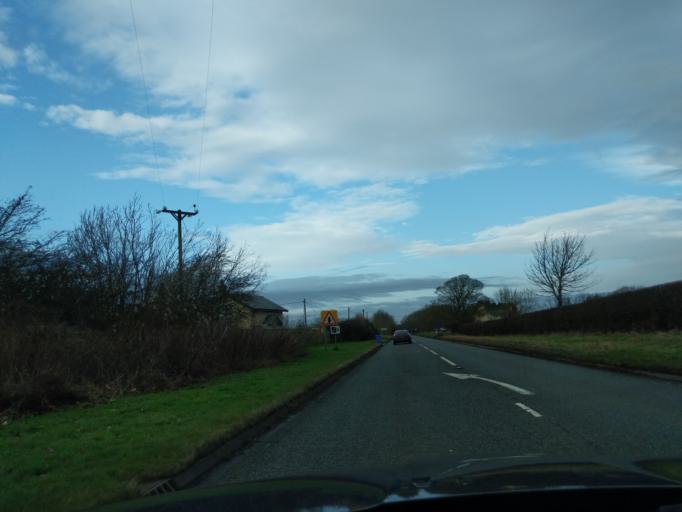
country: GB
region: England
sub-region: Northumberland
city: Darras Hall
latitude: 55.0747
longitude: -1.7972
